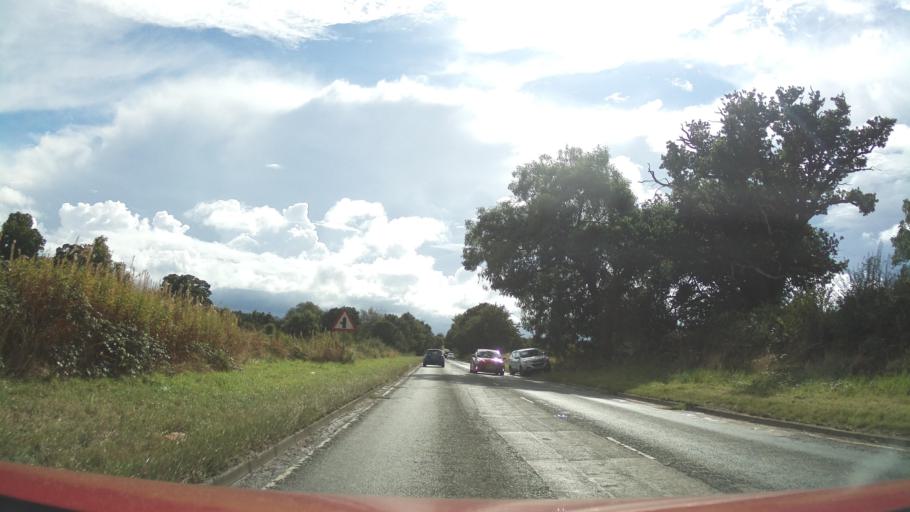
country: GB
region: England
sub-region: Shropshire
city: Shifnal
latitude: 52.6526
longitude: -2.3985
